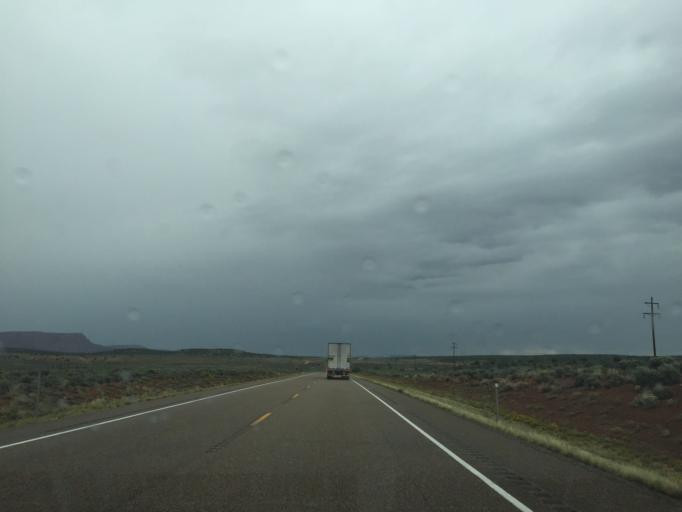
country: US
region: Utah
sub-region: Kane County
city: Kanab
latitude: 37.1249
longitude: -112.0975
